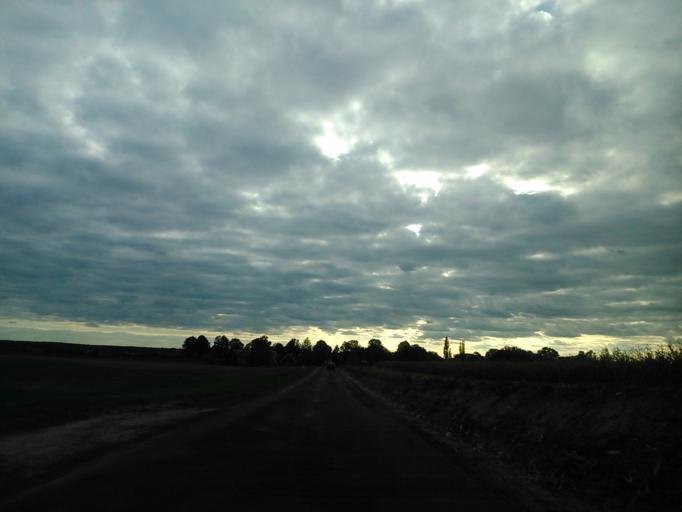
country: PL
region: Kujawsko-Pomorskie
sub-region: Powiat golubsko-dobrzynski
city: Kowalewo Pomorskie
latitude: 53.1327
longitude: 18.9488
